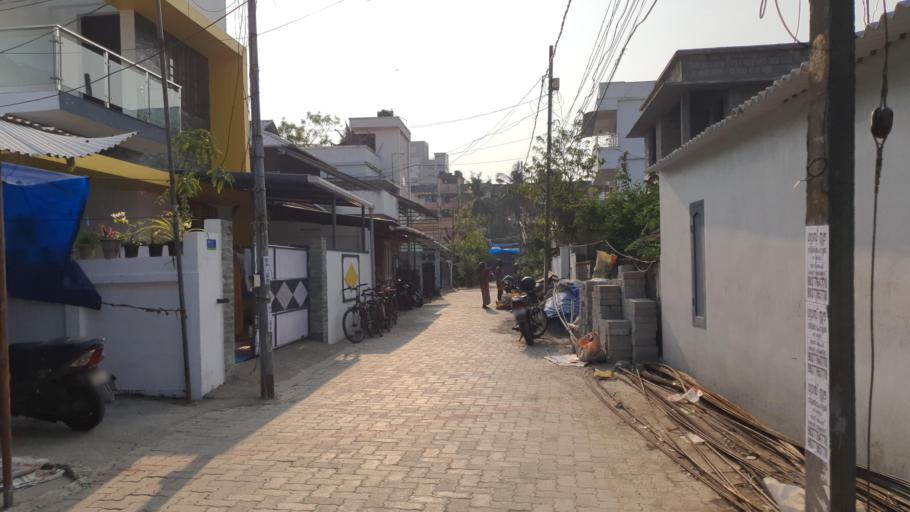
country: IN
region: Kerala
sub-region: Ernakulam
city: Cochin
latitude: 9.9584
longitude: 76.2997
